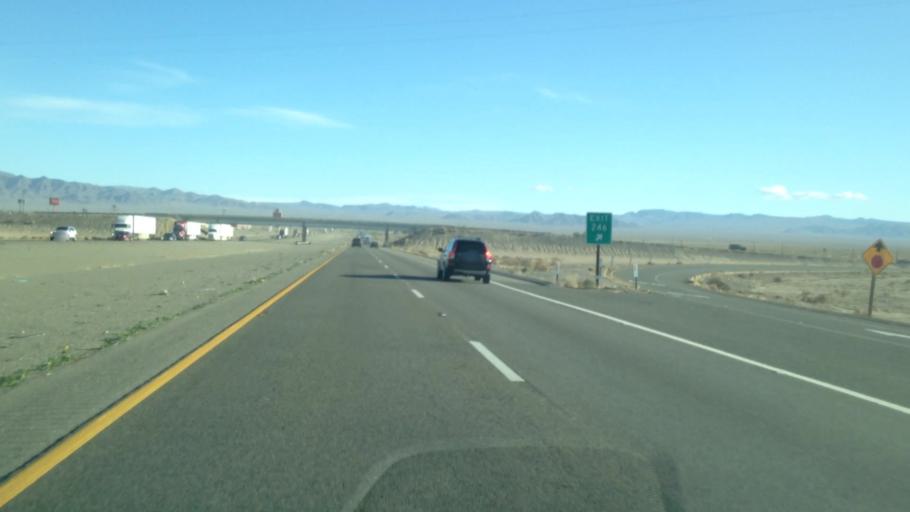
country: US
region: California
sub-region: San Bernardino County
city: Fort Irwin
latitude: 35.2616
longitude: -116.0758
